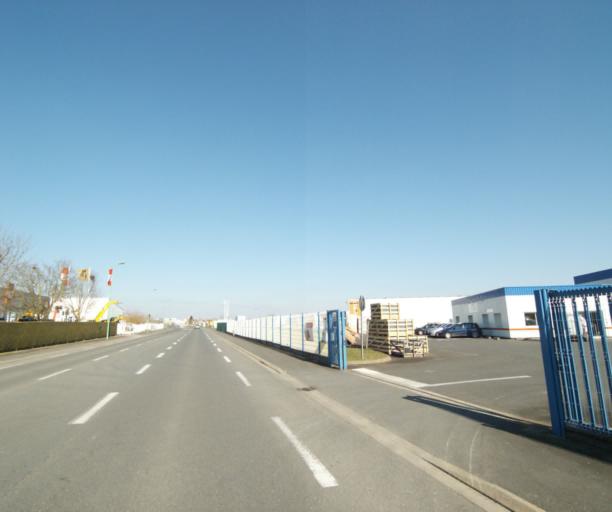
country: FR
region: Poitou-Charentes
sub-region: Departement des Deux-Sevres
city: Aiffres
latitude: 46.3311
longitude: -0.4089
